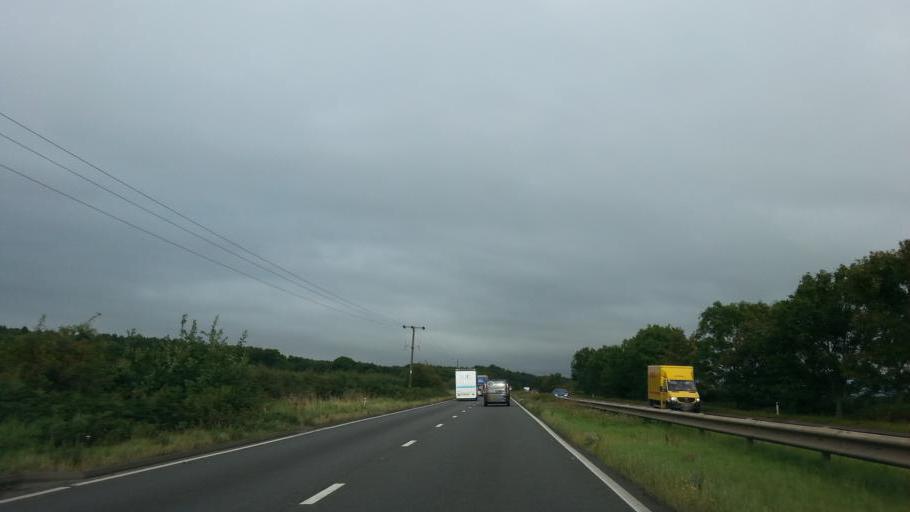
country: GB
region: England
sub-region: Nottinghamshire
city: Babworth
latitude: 53.2889
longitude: -1.0136
